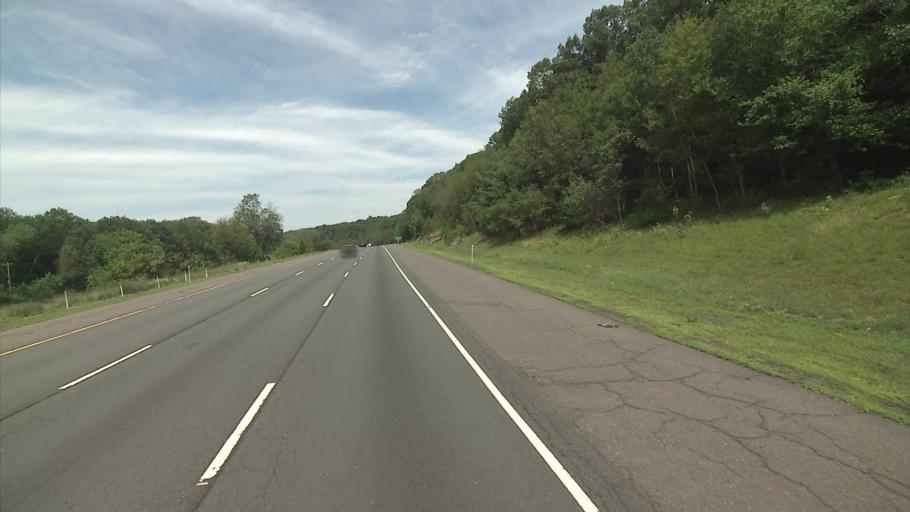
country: US
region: Connecticut
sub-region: Tolland County
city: Tolland
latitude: 41.8545
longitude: -72.3937
